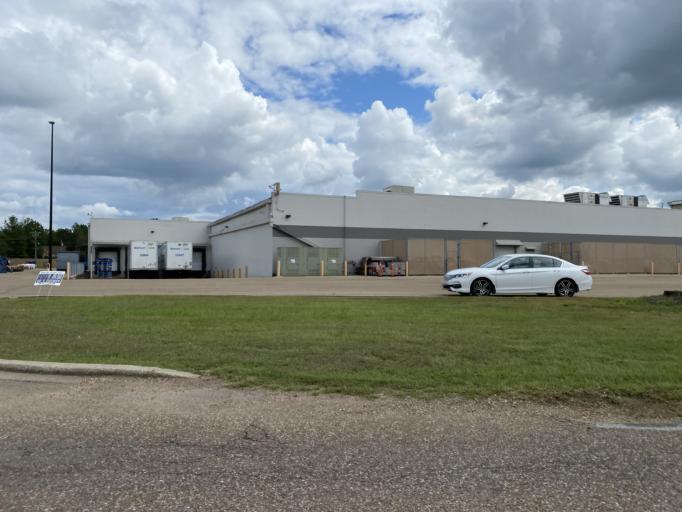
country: US
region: Mississippi
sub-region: Monroe County
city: Amory
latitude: 33.9698
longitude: -88.4575
